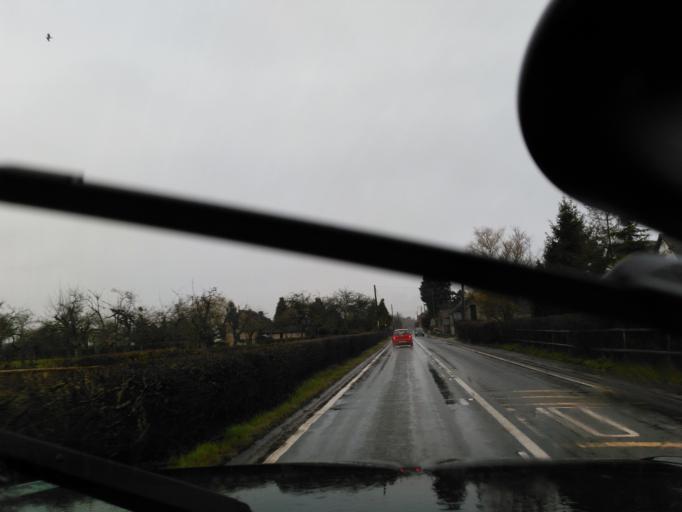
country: GB
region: England
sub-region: Somerset
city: Glastonbury
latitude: 51.1389
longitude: -2.6656
